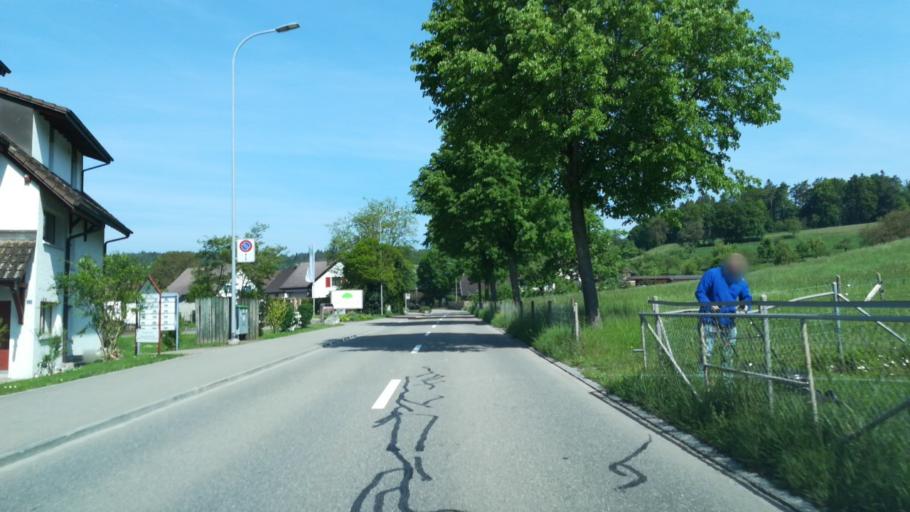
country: CH
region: Thurgau
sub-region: Frauenfeld District
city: Pfyn
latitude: 47.5999
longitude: 8.9519
